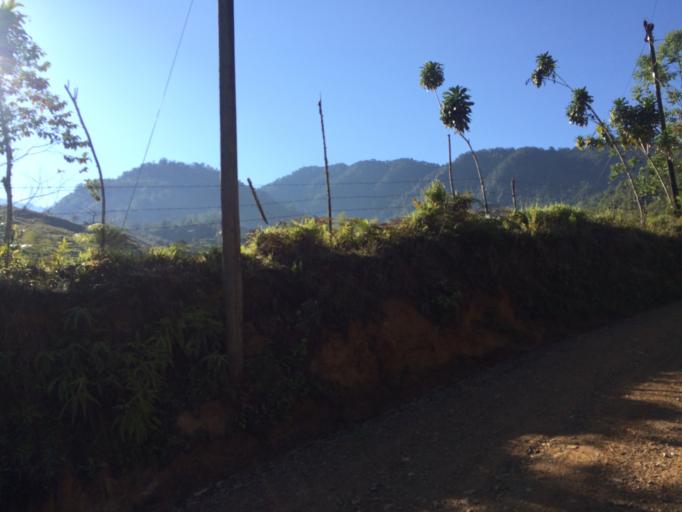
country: CR
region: San Jose
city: San Isidro
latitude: 9.4548
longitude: -83.5964
